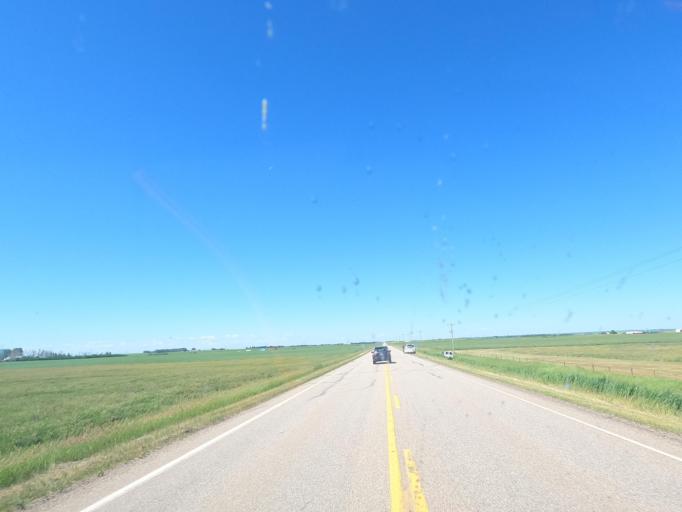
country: CA
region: Alberta
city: Irricana
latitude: 51.1543
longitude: -113.6474
